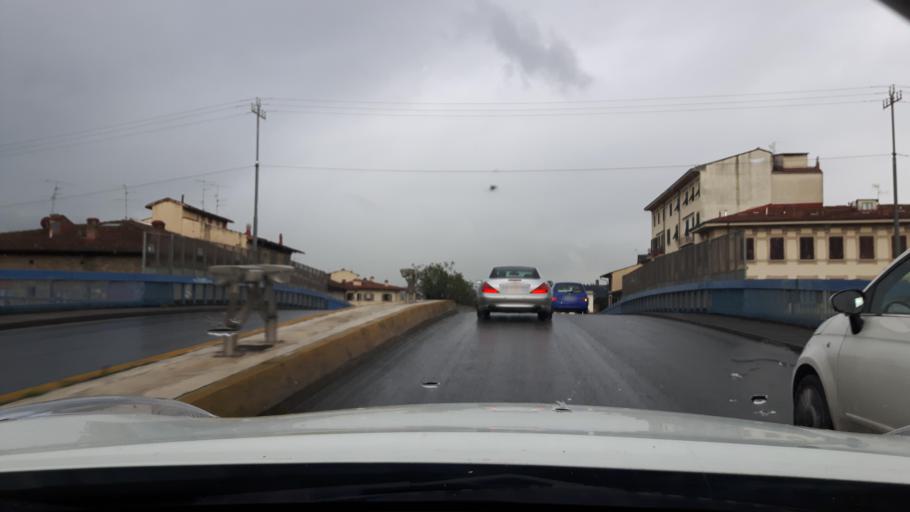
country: IT
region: Tuscany
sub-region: Province of Florence
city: Fiesole
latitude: 43.7714
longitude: 11.2830
